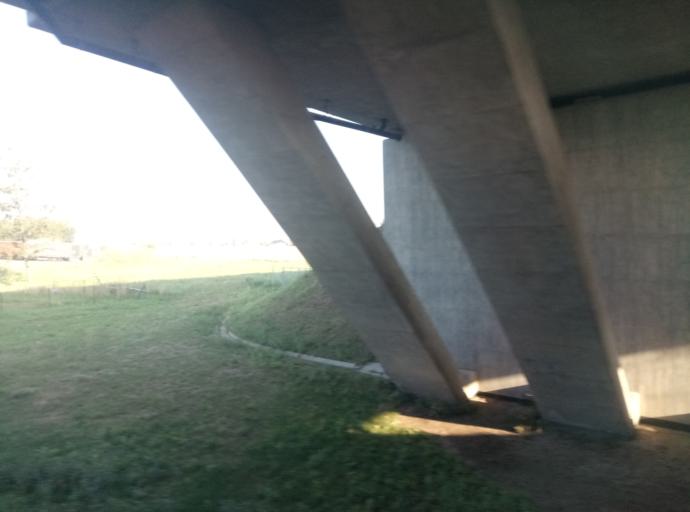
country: PL
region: Kujawsko-Pomorskie
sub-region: Powiat torunski
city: Lubicz Dolny
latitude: 53.1085
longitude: 18.7472
